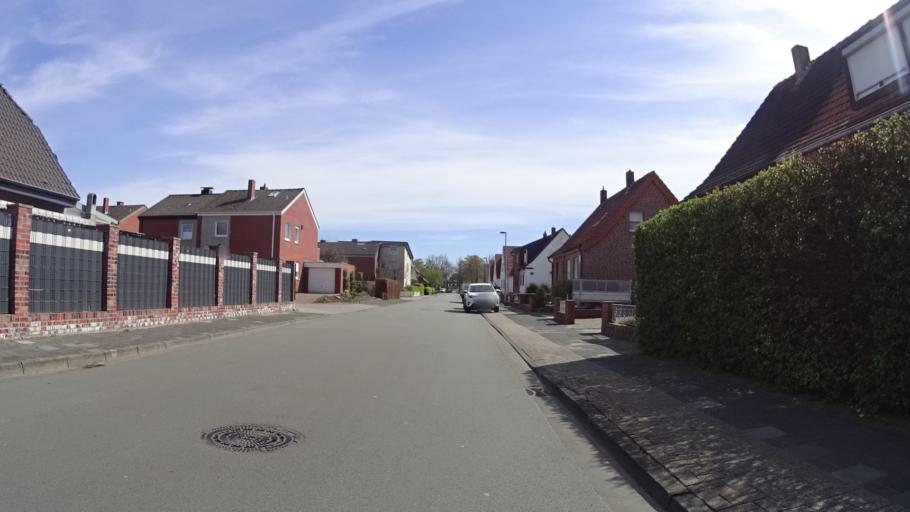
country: DE
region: North Rhine-Westphalia
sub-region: Regierungsbezirk Munster
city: Dreierwalde
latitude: 52.2897
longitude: 7.4726
